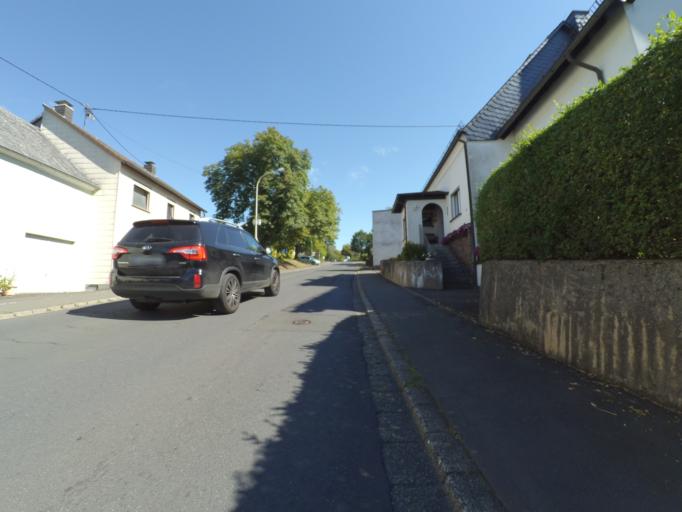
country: DE
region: Rheinland-Pfalz
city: Saxler
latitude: 50.1303
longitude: 6.9093
